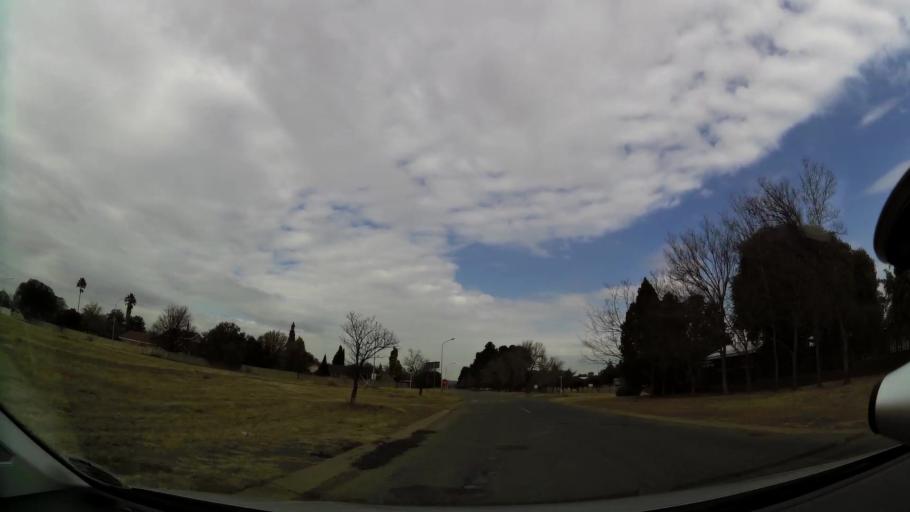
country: ZA
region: Orange Free State
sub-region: Fezile Dabi District Municipality
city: Kroonstad
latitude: -27.6316
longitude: 27.2384
